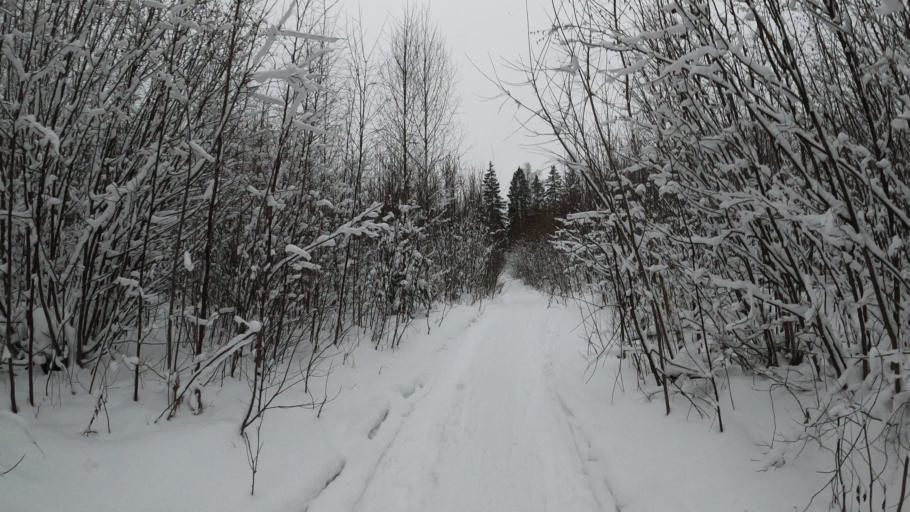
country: RU
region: Moskovskaya
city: Firsanovka
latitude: 55.9110
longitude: 37.2038
